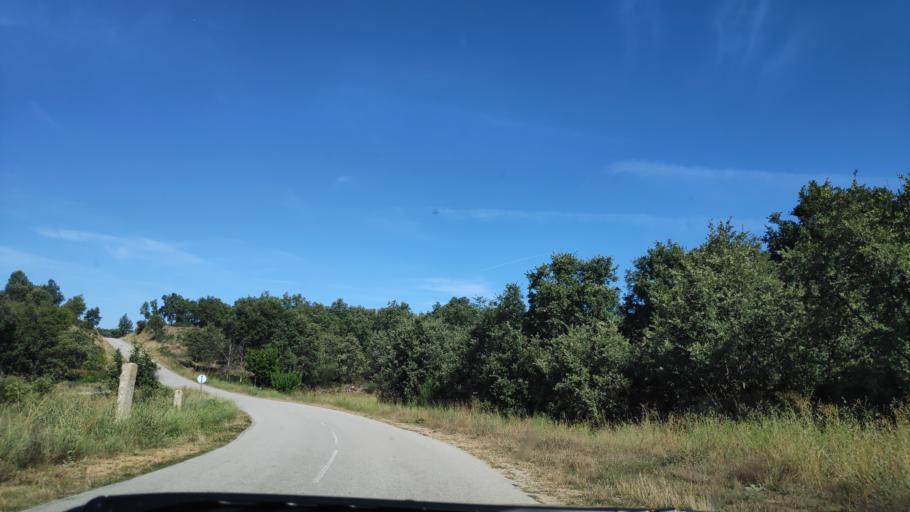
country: ES
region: Castille and Leon
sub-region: Provincia de Zamora
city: Alcanices
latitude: 41.6422
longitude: -6.3552
